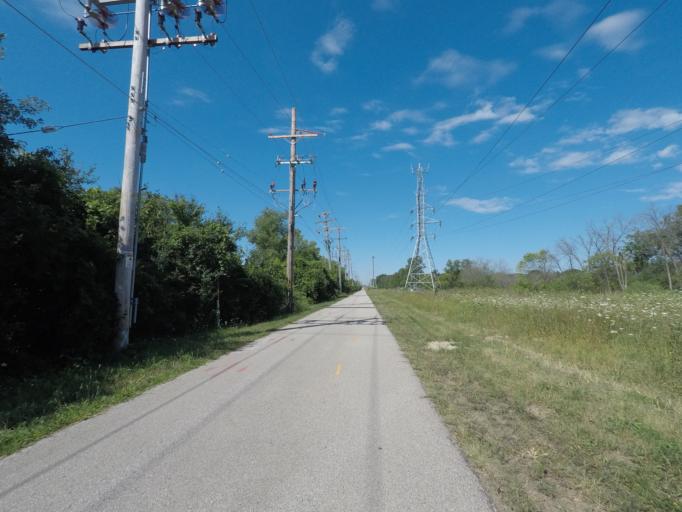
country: US
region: Wisconsin
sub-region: Waukesha County
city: Waukesha
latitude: 43.0099
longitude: -88.1752
